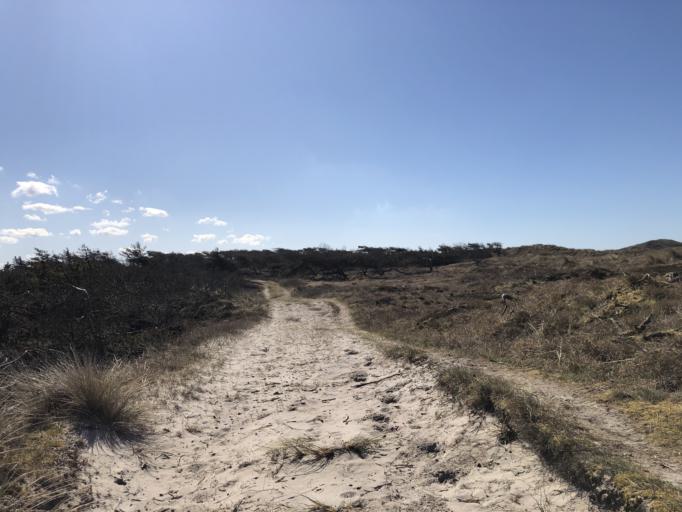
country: DK
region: Central Jutland
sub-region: Holstebro Kommune
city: Ulfborg
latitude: 56.3063
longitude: 8.1295
